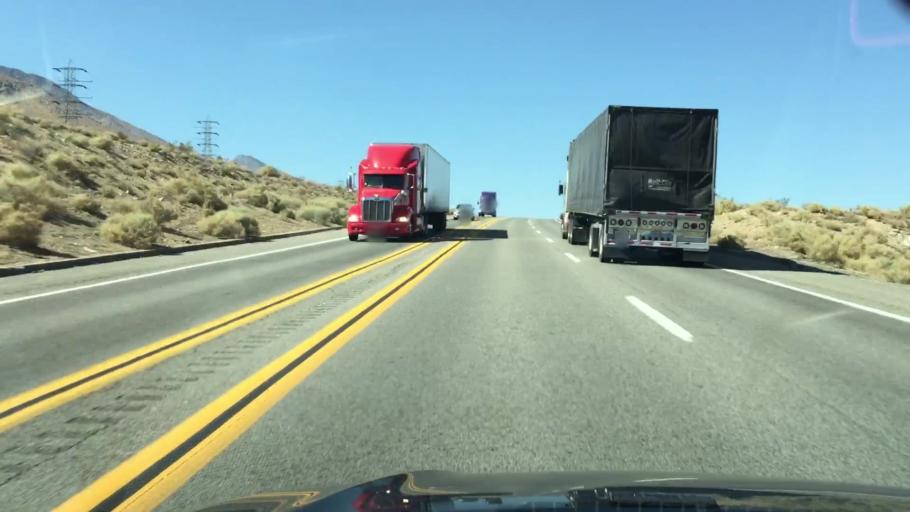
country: US
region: California
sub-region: Inyo County
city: Lone Pine
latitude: 36.3517
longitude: -118.0250
